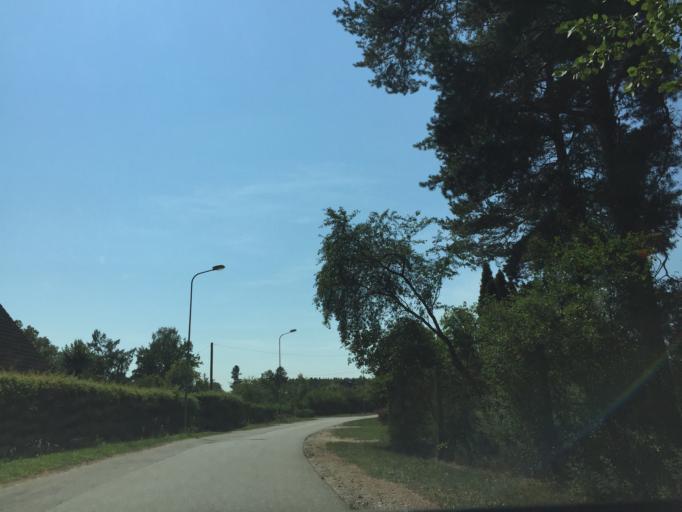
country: LV
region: Babite
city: Pinki
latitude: 56.9548
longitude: 23.9437
